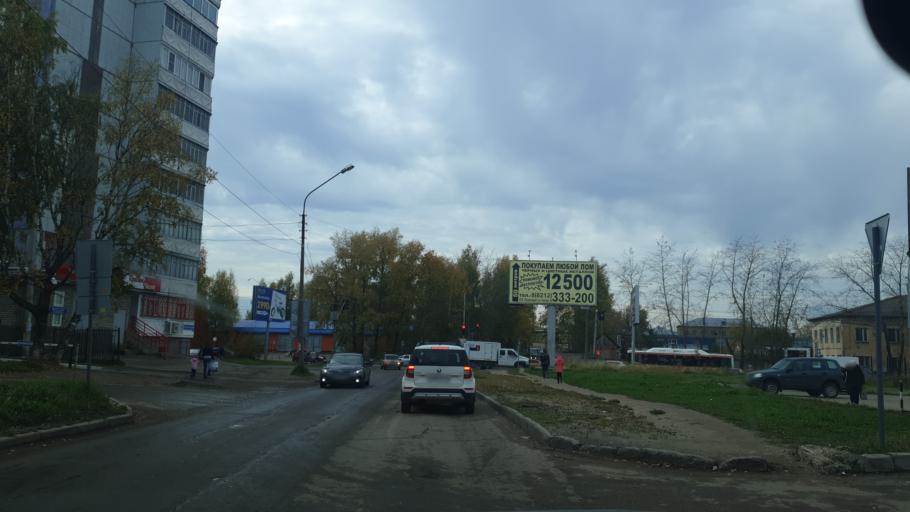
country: RU
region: Komi Republic
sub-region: Syktyvdinskiy Rayon
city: Syktyvkar
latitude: 61.6781
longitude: 50.8102
